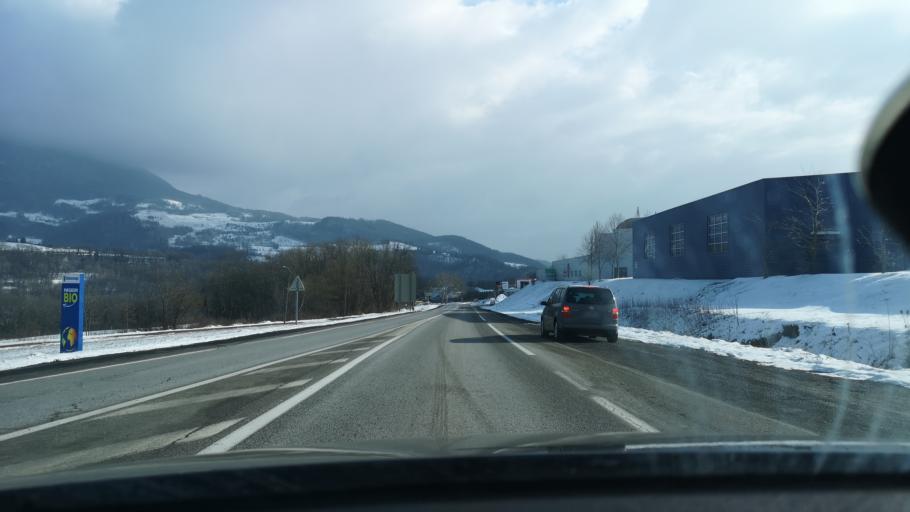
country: FR
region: Rhone-Alpes
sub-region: Departement de l'Ain
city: Chatillon-en-Michaille
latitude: 46.1278
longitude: 5.8126
